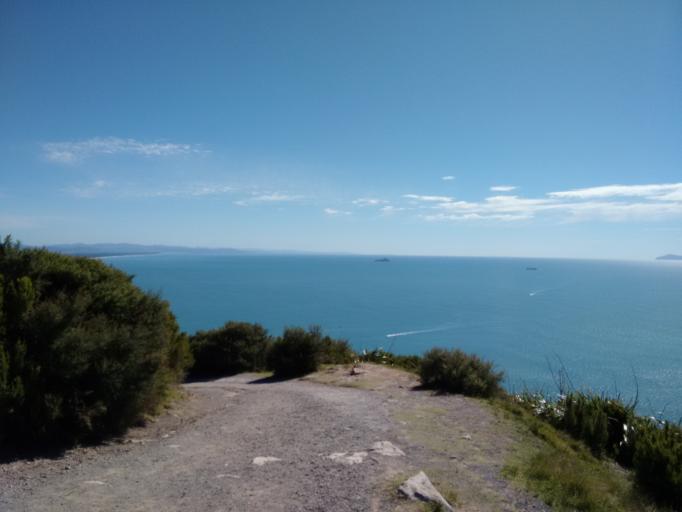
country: NZ
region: Bay of Plenty
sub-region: Tauranga City
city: Tauranga
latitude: -37.6287
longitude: 176.1714
